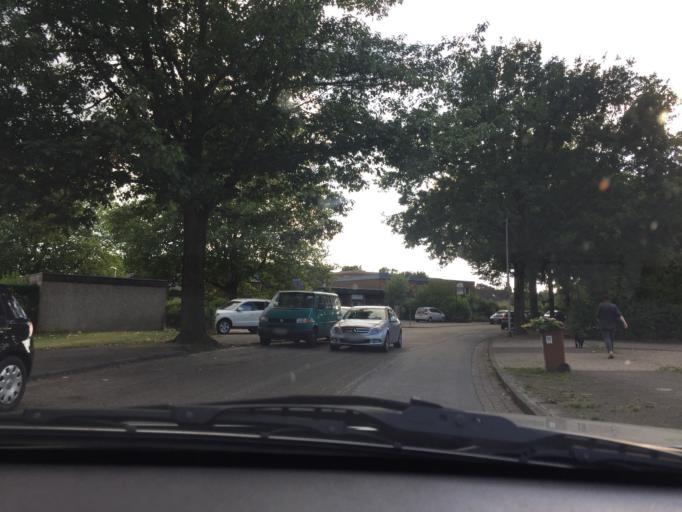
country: DE
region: North Rhine-Westphalia
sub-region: Regierungsbezirk Dusseldorf
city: Kleve
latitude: 51.7681
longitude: 6.1106
